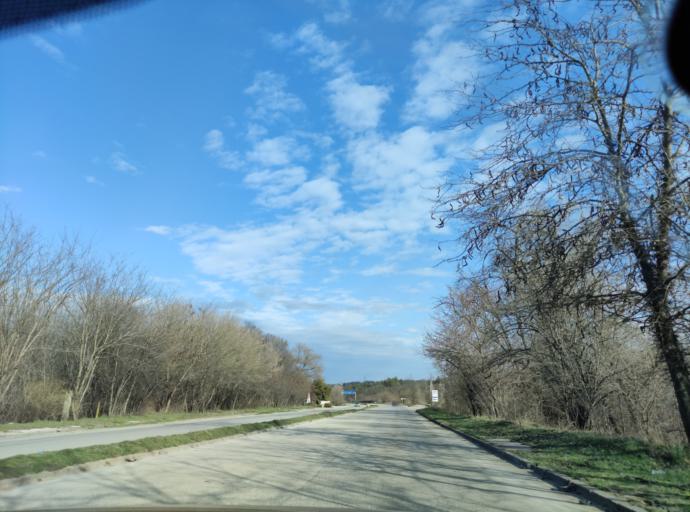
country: BG
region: Pleven
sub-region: Obshtina Dolna Mitropoliya
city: Dolna Mitropoliya
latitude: 43.4330
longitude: 24.5442
